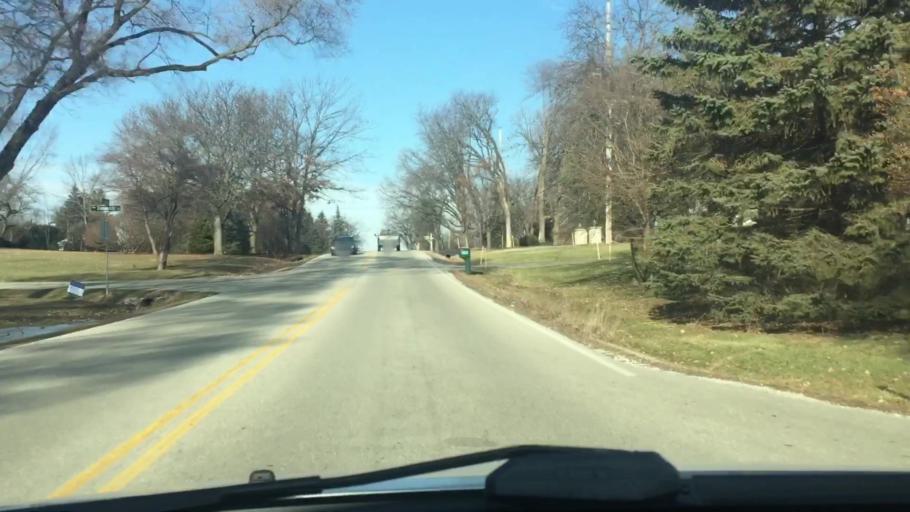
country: US
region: Wisconsin
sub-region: Waukesha County
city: Elm Grove
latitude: 43.0551
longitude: -88.0668
